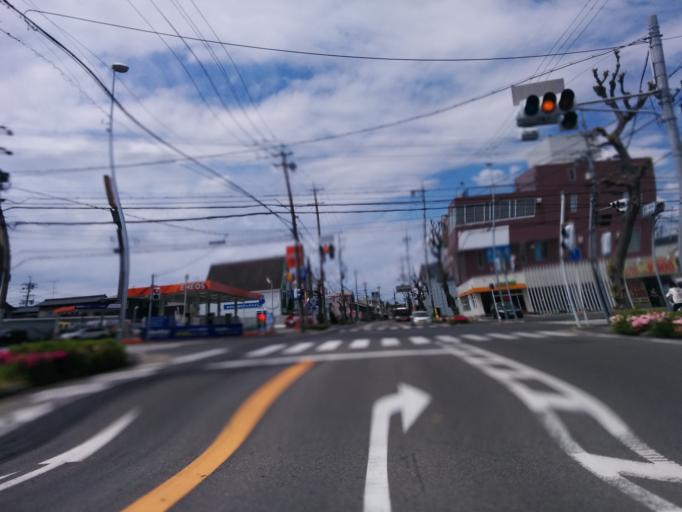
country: JP
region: Aichi
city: Kasugai
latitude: 35.2575
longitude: 136.9754
